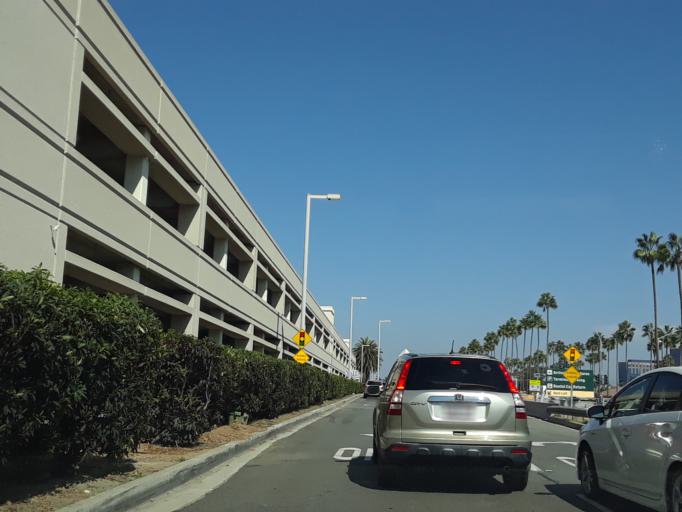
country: US
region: California
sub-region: Orange County
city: Irvine
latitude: 33.6771
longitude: -117.8644
